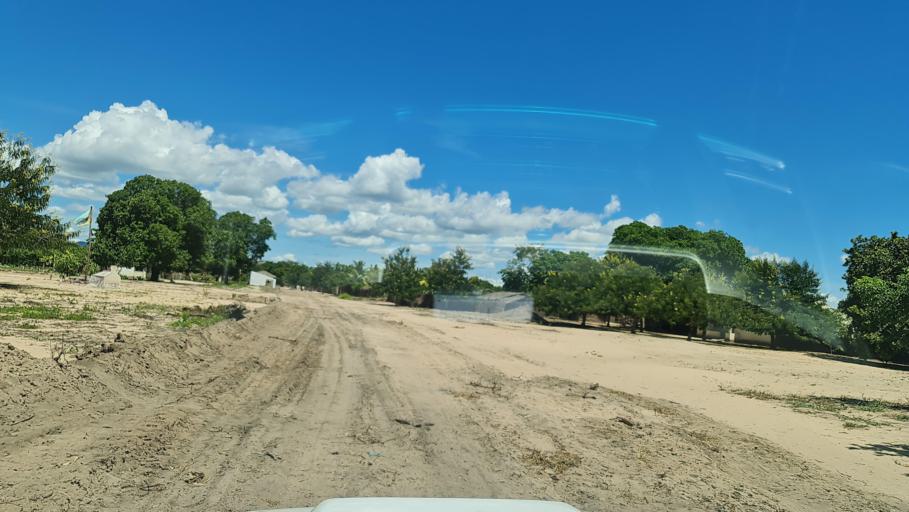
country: MZ
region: Nampula
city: Nampula
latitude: -15.2999
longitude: 39.8689
